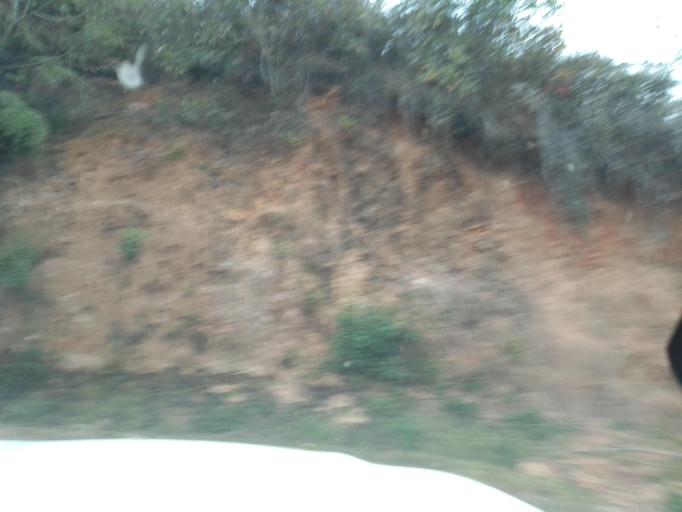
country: MX
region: Chiapas
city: Motozintla de Mendoza
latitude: 15.2108
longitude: -92.2250
